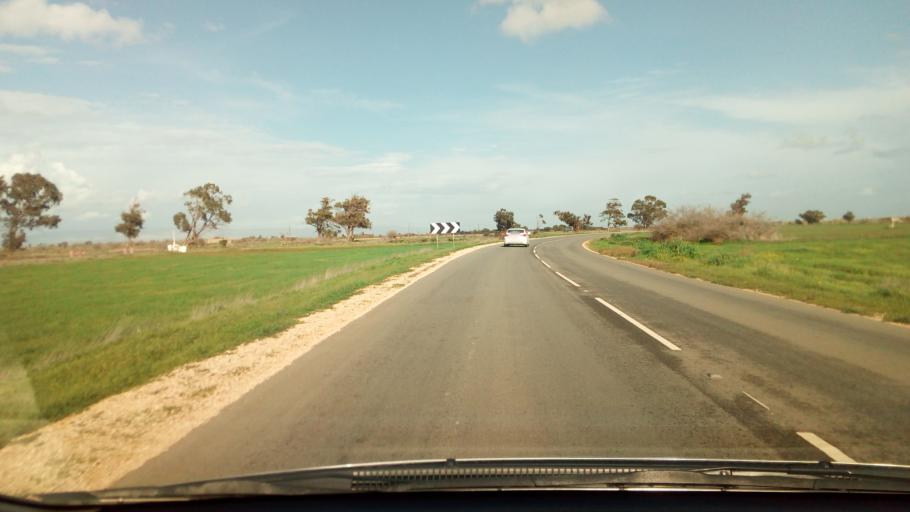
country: CY
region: Ammochostos
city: Achna
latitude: 35.0582
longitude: 33.7964
